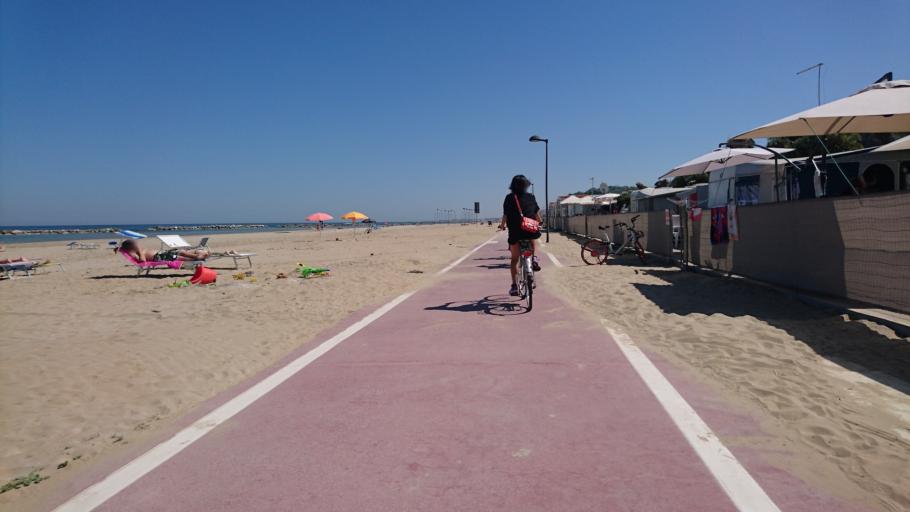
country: IT
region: The Marches
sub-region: Provincia di Pesaro e Urbino
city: Fenile
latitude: 43.8853
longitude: 12.9573
